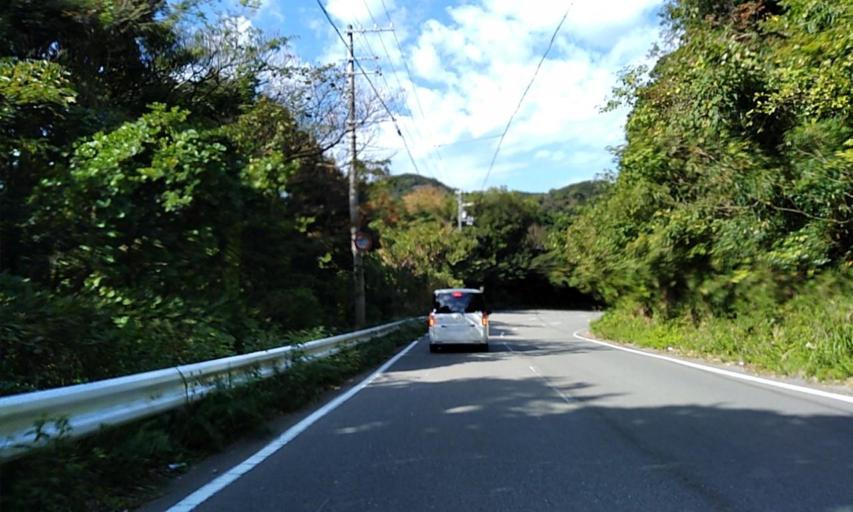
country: JP
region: Wakayama
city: Gobo
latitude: 33.9665
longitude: 135.1185
